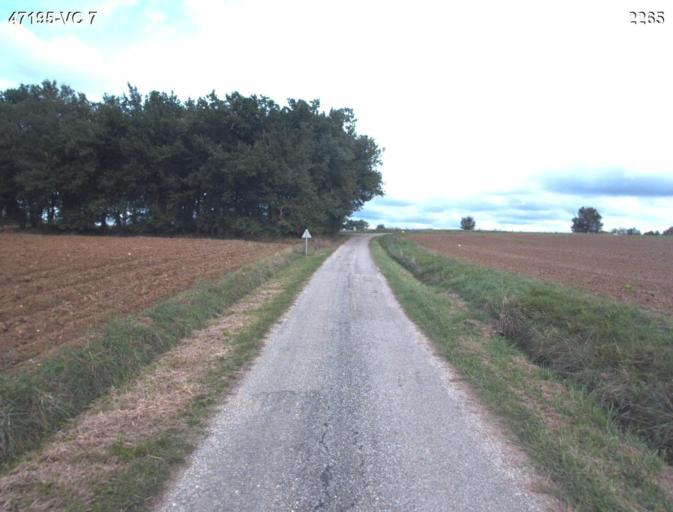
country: FR
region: Aquitaine
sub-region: Departement du Lot-et-Garonne
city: Nerac
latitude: 44.0983
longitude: 0.3367
